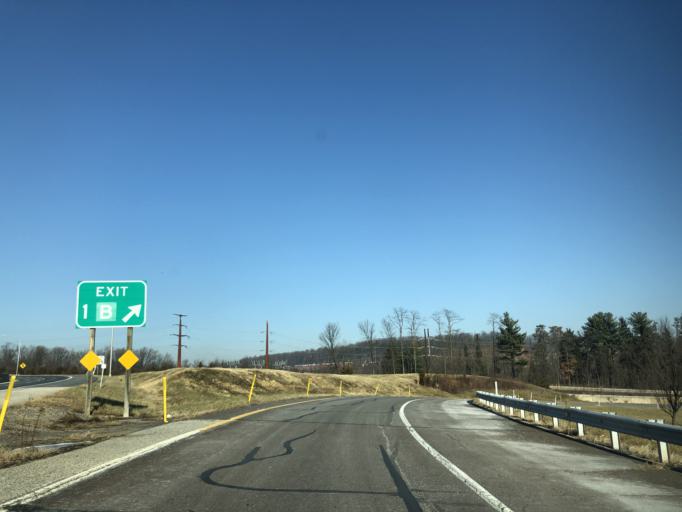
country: US
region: Pennsylvania
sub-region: Chester County
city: Elverson
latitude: 40.1646
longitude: -75.8832
